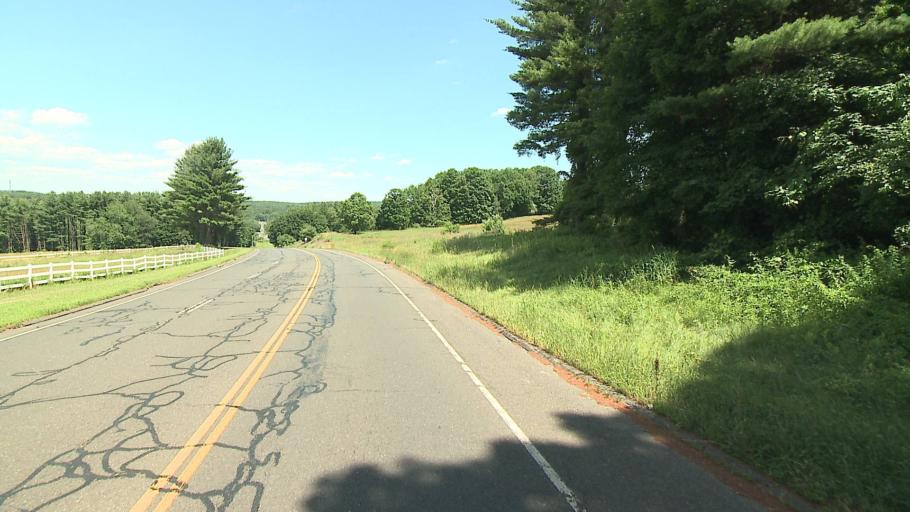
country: US
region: Connecticut
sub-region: Fairfield County
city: Newtown
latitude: 41.4037
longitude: -73.2813
